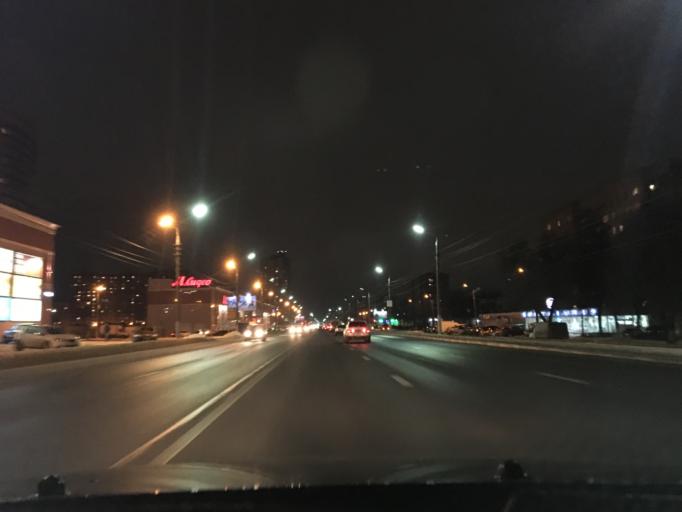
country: RU
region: Tula
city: Mendeleyevskiy
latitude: 54.1500
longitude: 37.5834
